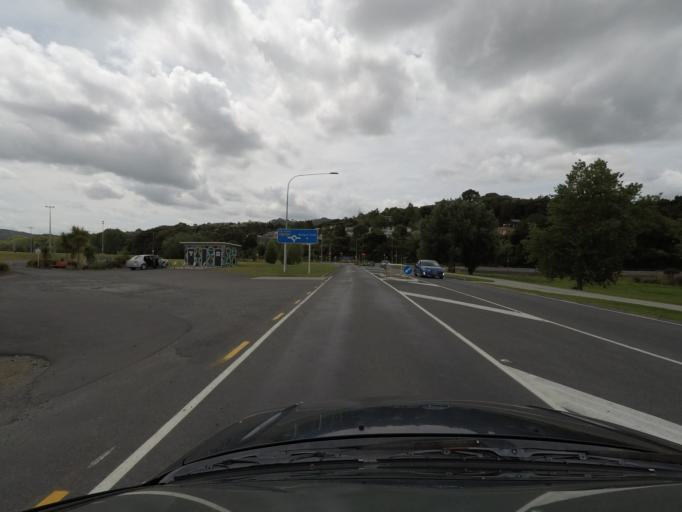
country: NZ
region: Northland
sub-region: Whangarei
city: Whangarei
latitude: -35.7324
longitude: 174.3428
